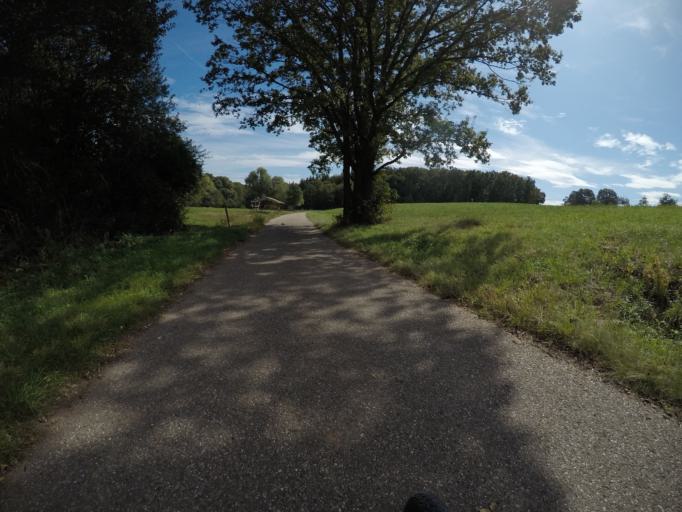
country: DE
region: Baden-Wuerttemberg
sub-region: Karlsruhe Region
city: Sternenfels
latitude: 49.0177
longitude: 8.8568
